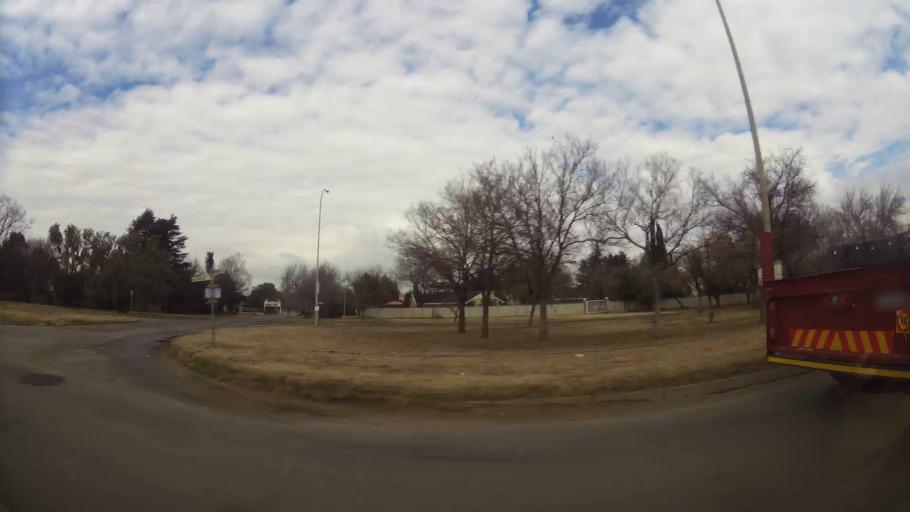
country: ZA
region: Gauteng
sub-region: Sedibeng District Municipality
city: Vereeniging
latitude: -26.6513
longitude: 27.9945
